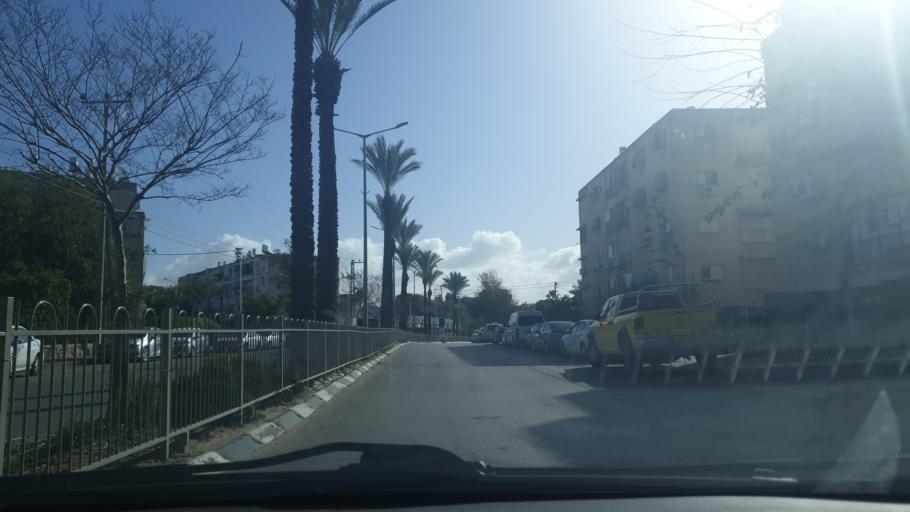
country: IL
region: Central District
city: Ramla
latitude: 31.9343
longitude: 34.8597
